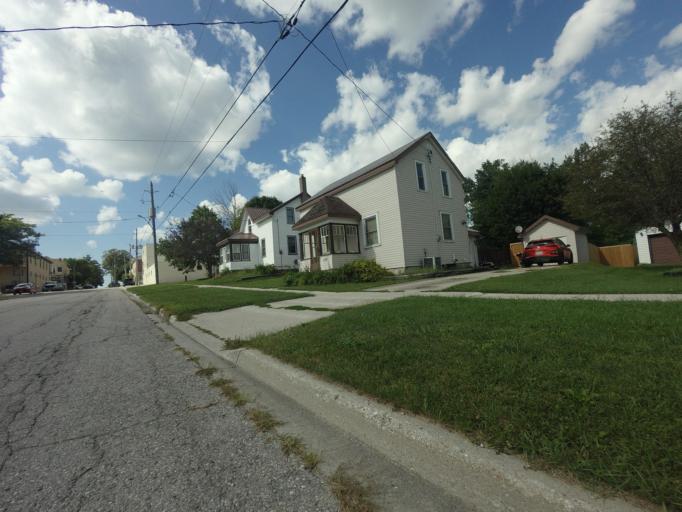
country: CA
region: Ontario
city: Huron East
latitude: 43.7360
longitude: -81.4282
